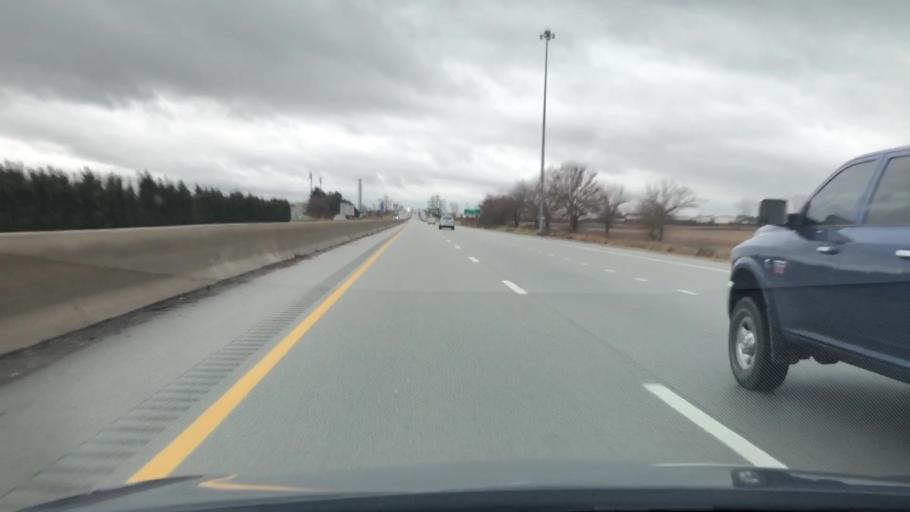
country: US
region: Ohio
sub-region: Wood County
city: Northwood
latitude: 41.6064
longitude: -83.4742
